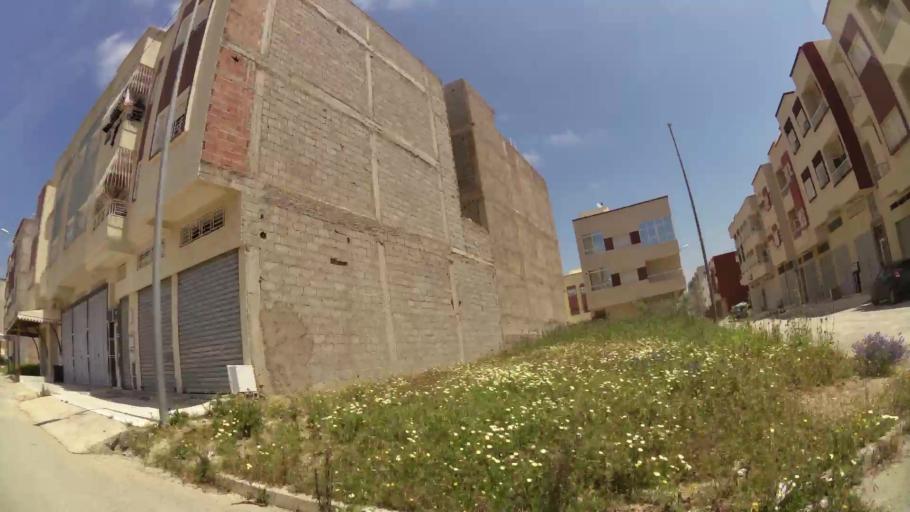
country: MA
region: Fes-Boulemane
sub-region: Fes
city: Fes
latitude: 34.0493
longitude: -5.0435
